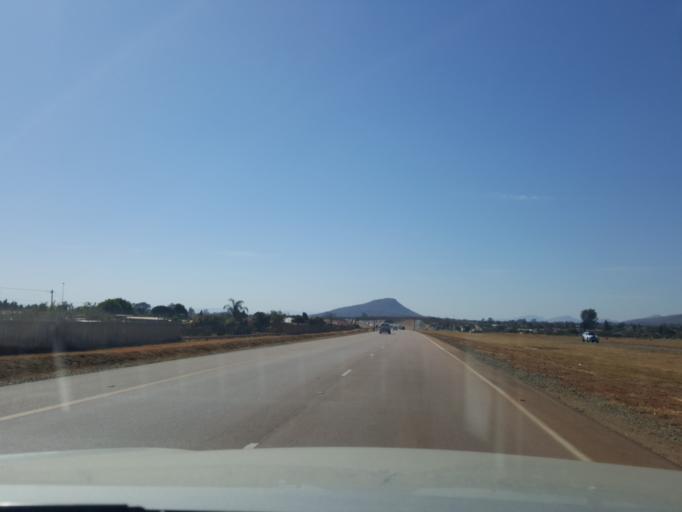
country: ZA
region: North-West
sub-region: Bojanala Platinum District Municipality
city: Brits
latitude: -25.7339
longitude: 27.6534
